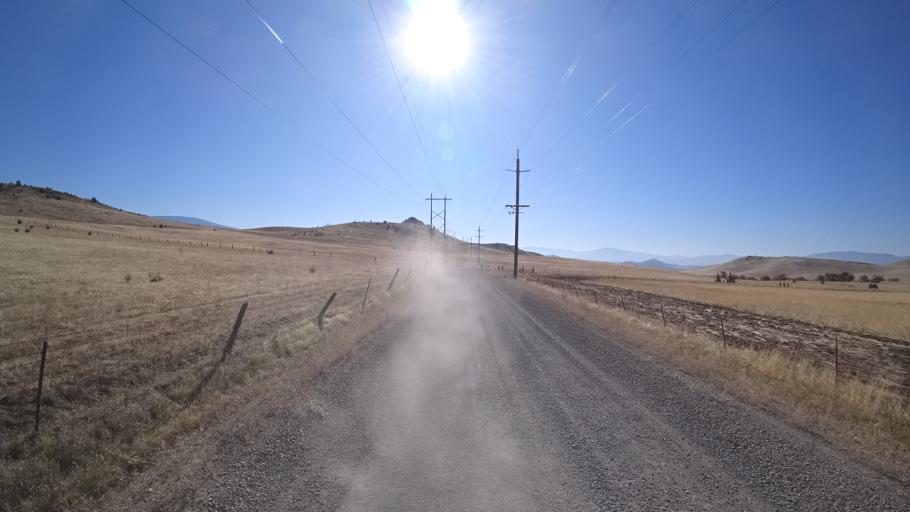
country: US
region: California
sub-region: Siskiyou County
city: Montague
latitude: 41.7503
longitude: -122.3595
